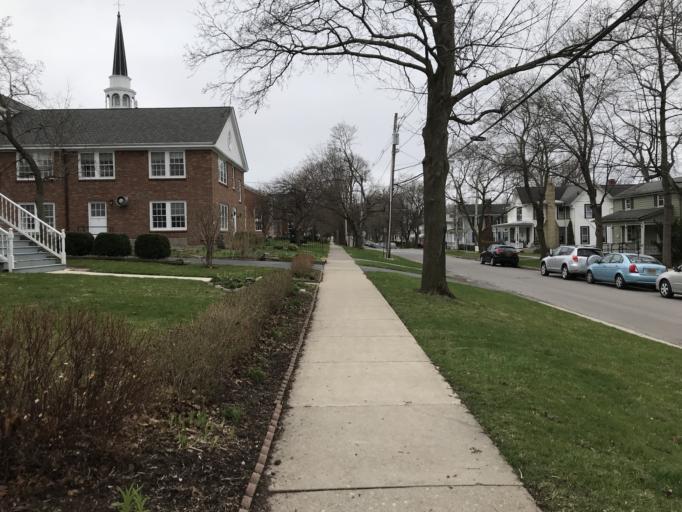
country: US
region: New York
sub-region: Livingston County
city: Geneseo
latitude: 42.7967
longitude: -77.8142
